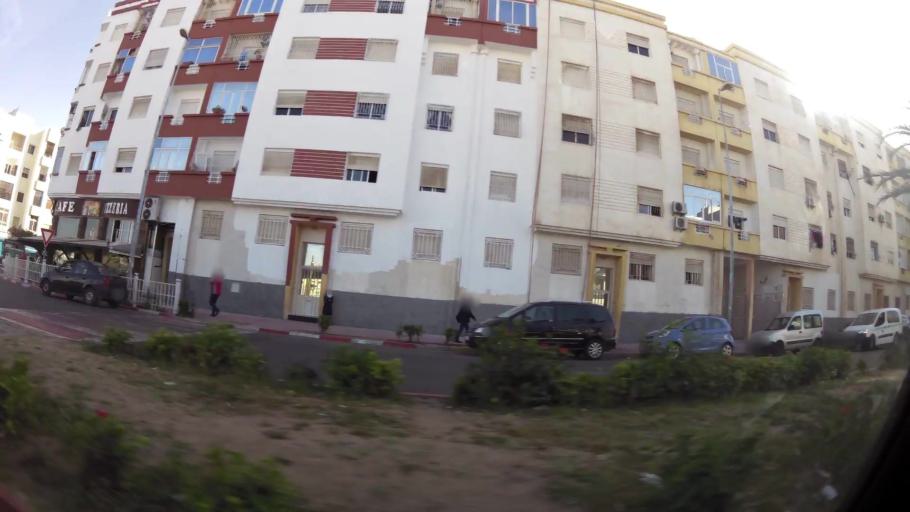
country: MA
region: Oued ed Dahab-Lagouira
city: Dakhla
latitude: 30.3993
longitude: -9.5512
